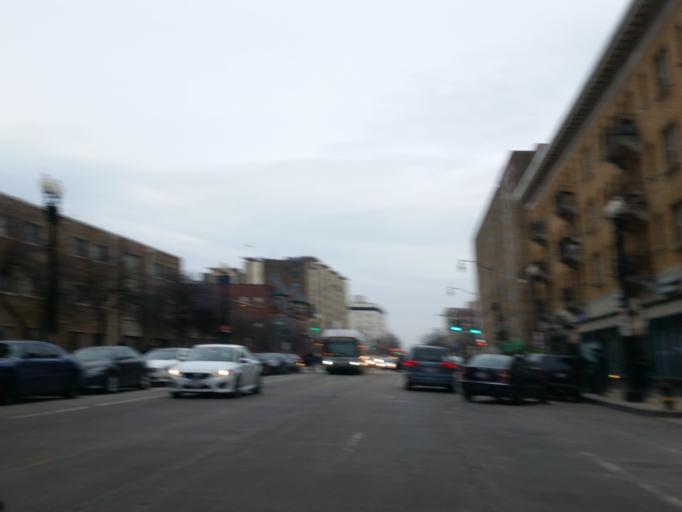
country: US
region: Washington, D.C.
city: Washington, D.C.
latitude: 38.9282
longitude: -77.0326
